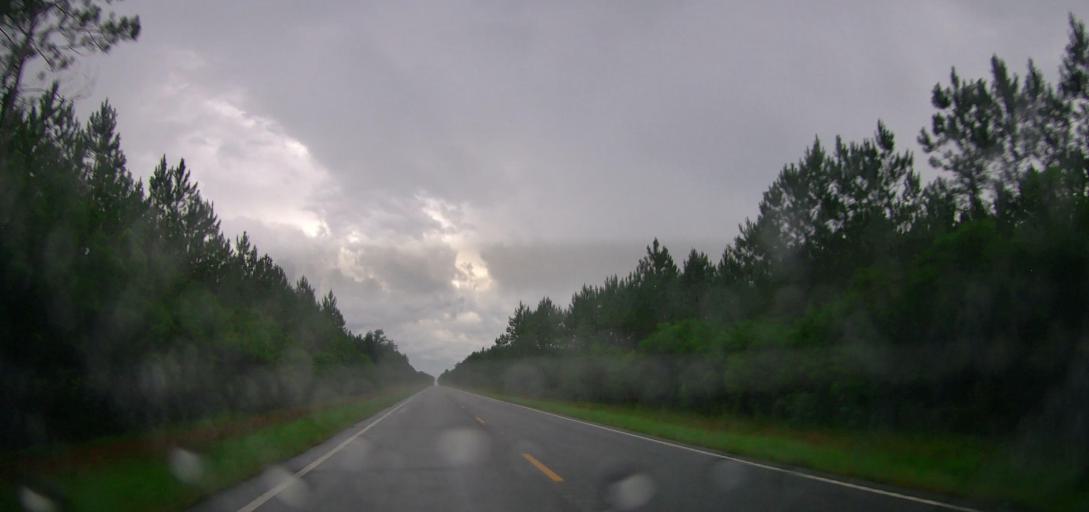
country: US
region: Georgia
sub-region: Brantley County
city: Nahunta
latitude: 31.3425
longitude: -81.8213
